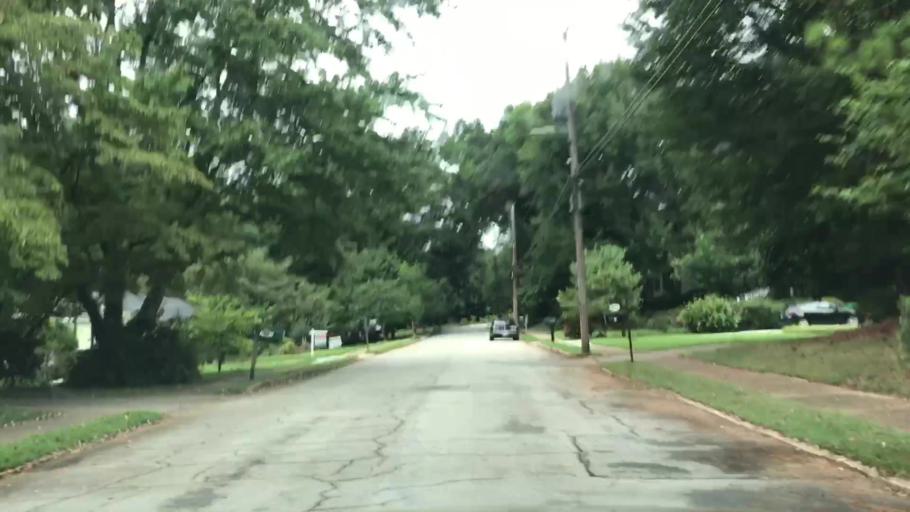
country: US
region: Georgia
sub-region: DeKalb County
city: Belvedere Park
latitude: 33.7630
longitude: -84.2715
